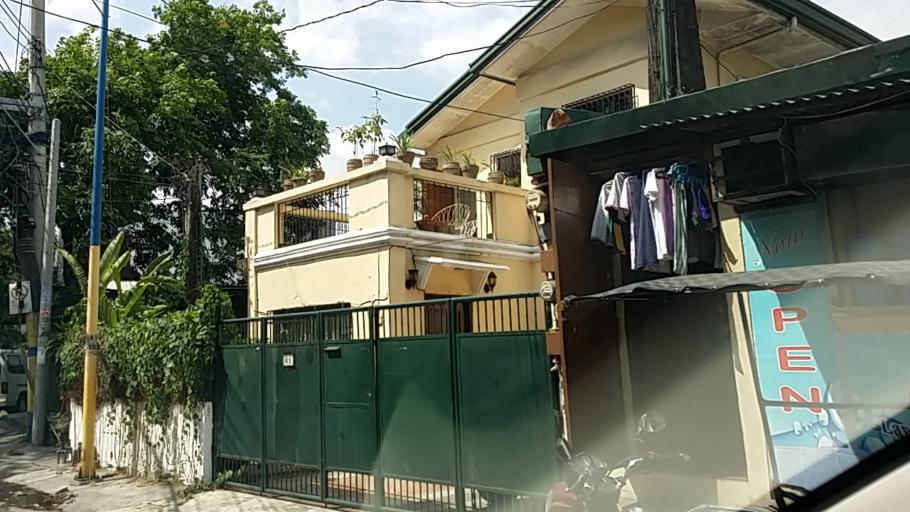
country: PH
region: Metro Manila
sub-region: Mandaluyong
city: Mandaluyong City
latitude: 14.5763
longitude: 121.0456
